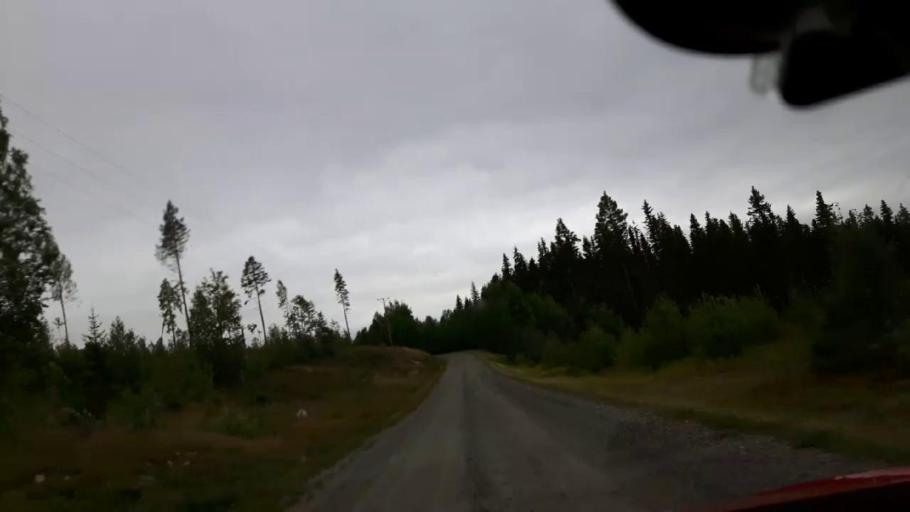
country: SE
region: Vaesternorrland
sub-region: Ange Kommun
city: Ange
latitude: 62.8560
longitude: 15.9128
